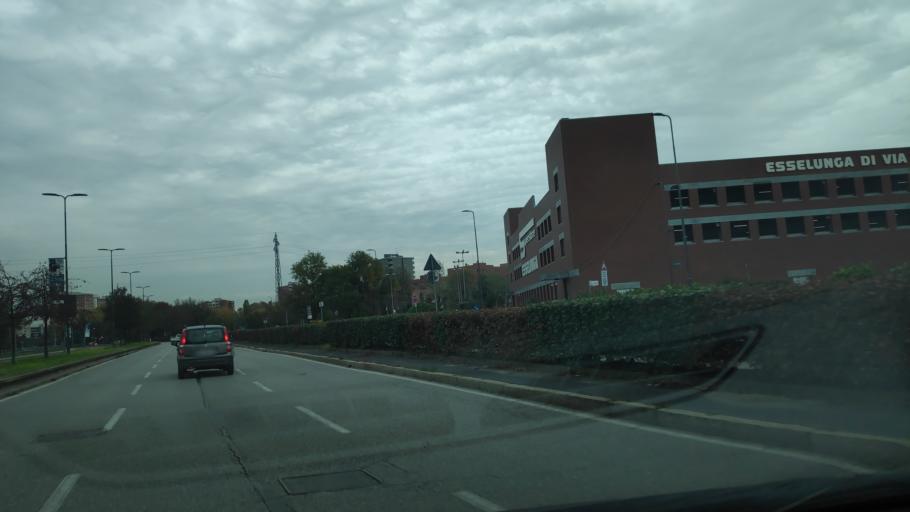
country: IT
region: Lombardy
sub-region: Citta metropolitana di Milano
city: Rozzano
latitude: 45.4203
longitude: 9.1762
